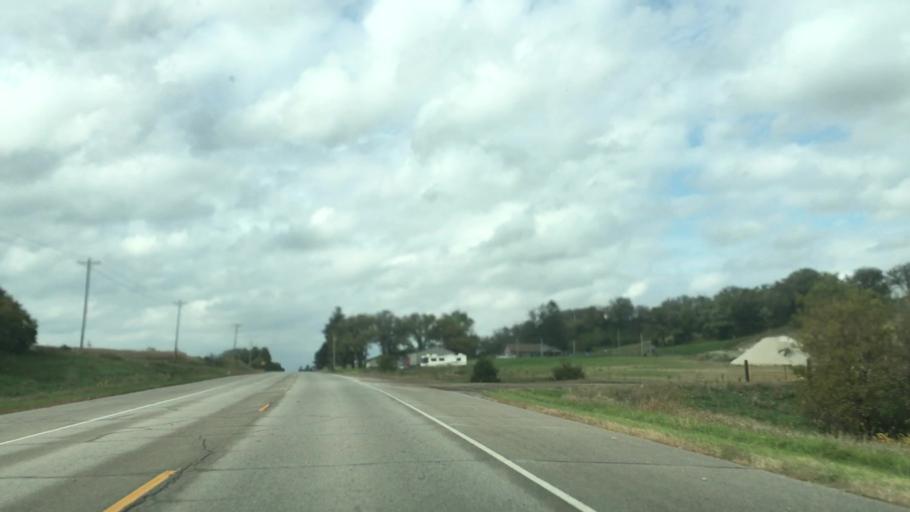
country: US
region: Minnesota
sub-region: Fillmore County
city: Chatfield
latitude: 43.8660
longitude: -92.2000
